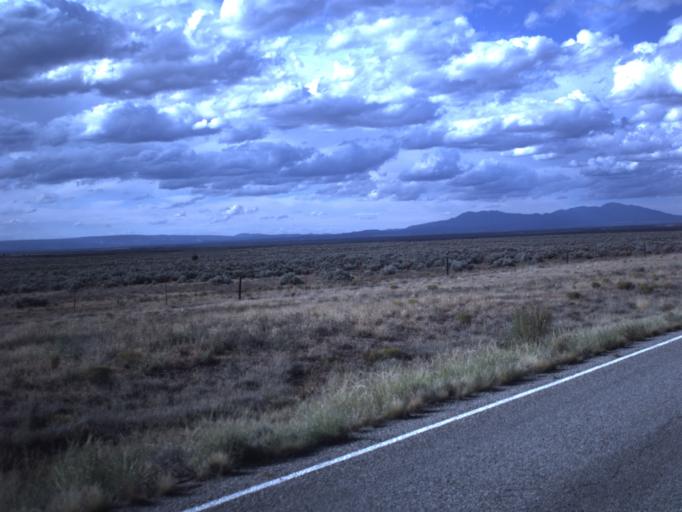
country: US
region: Utah
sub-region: San Juan County
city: Blanding
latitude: 37.3702
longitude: -109.3434
